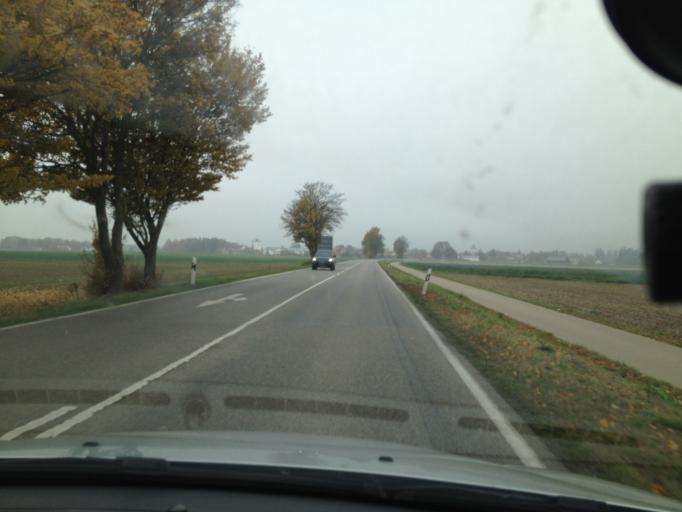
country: DE
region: Bavaria
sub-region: Swabia
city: Schwabmunchen
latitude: 48.1696
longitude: 10.7760
